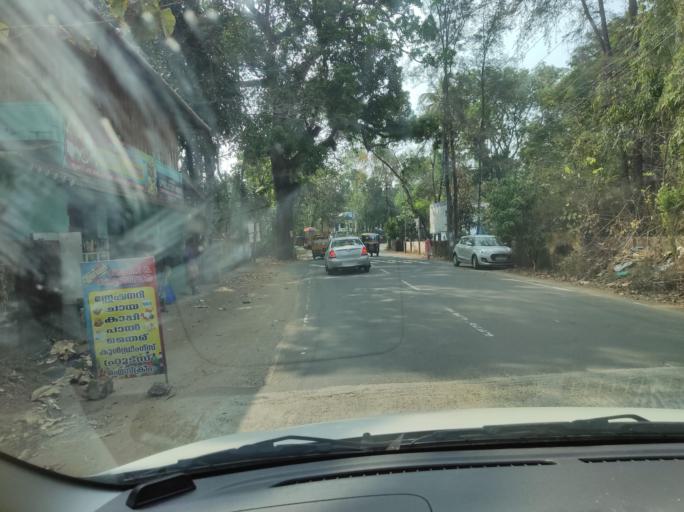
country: IN
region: Kerala
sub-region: Kottayam
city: Kottayam
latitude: 9.6758
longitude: 76.5449
